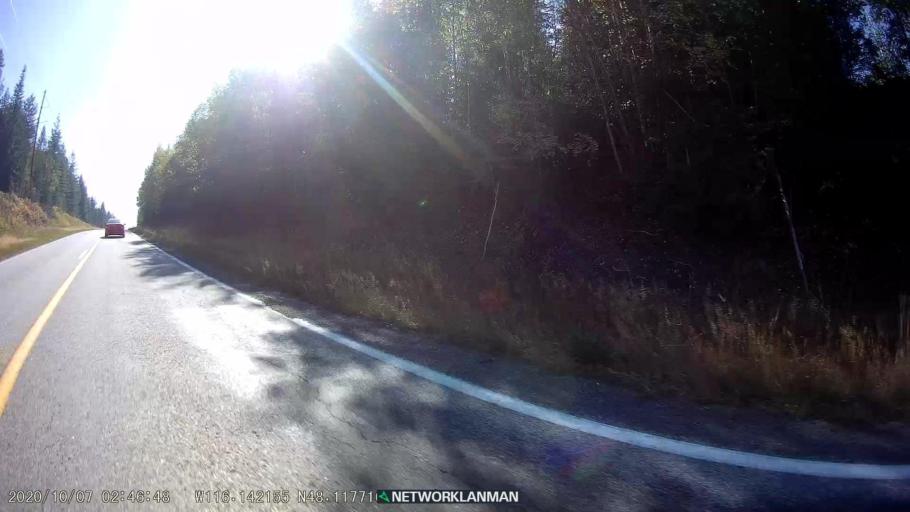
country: US
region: Idaho
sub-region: Bonner County
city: Ponderay
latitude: 48.1175
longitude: -116.1420
